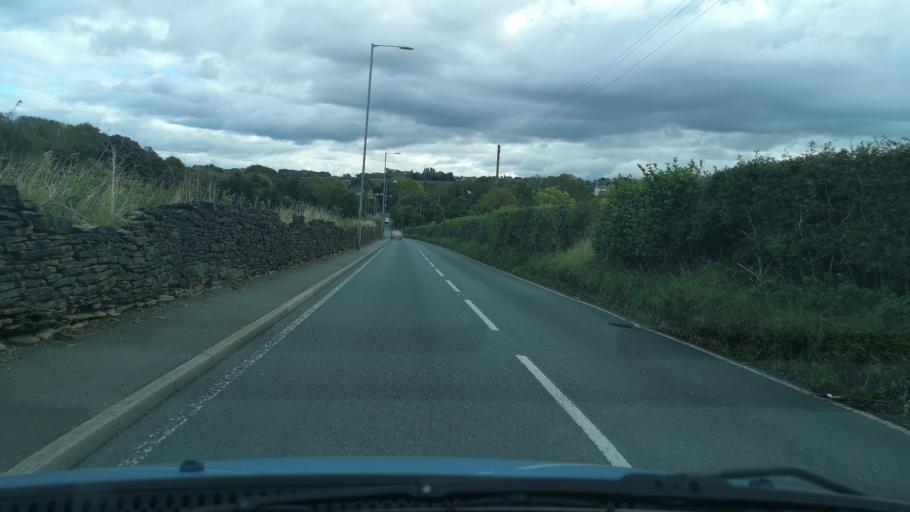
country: GB
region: England
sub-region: City and Borough of Wakefield
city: Middlestown
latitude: 53.6579
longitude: -1.5860
